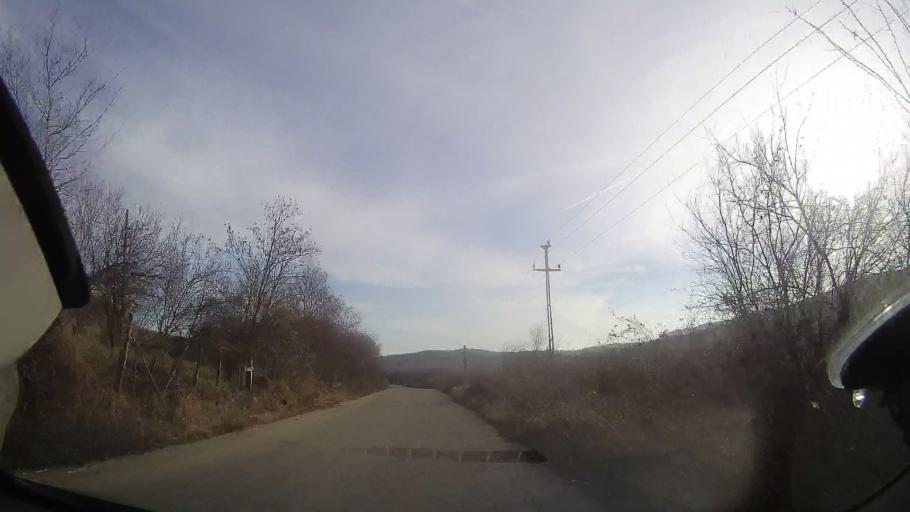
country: RO
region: Bihor
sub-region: Comuna Sarbi
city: Sarbi
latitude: 47.1841
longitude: 22.1306
